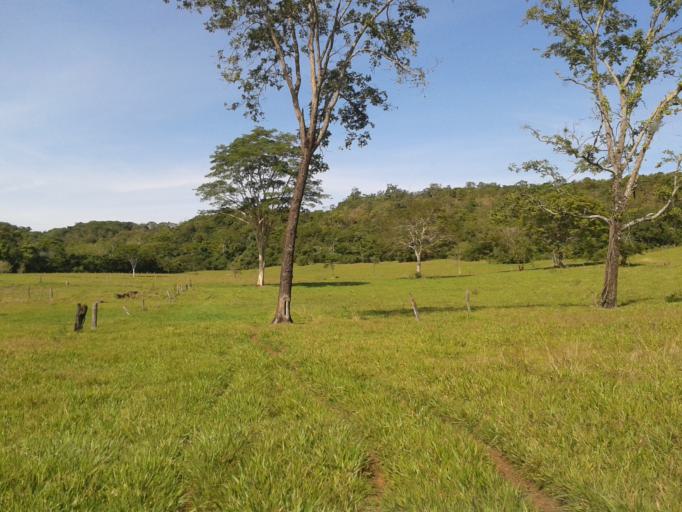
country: BR
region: Minas Gerais
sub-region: Campina Verde
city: Campina Verde
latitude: -19.4432
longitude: -49.6866
